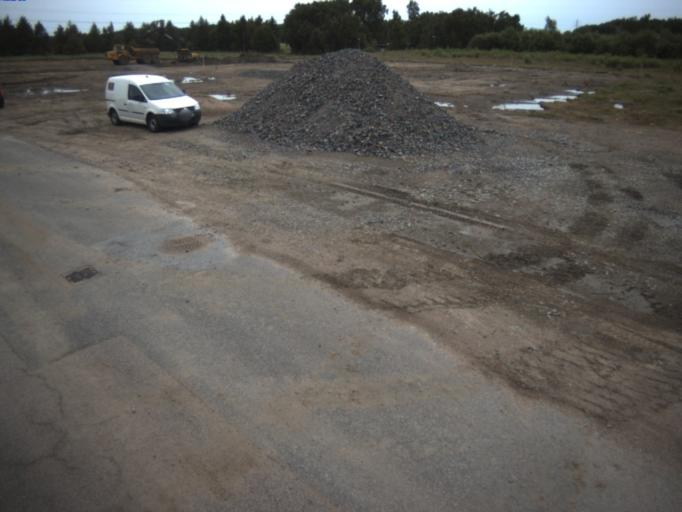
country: SE
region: Skane
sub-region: Helsingborg
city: Odakra
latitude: 56.0830
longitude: 12.7255
